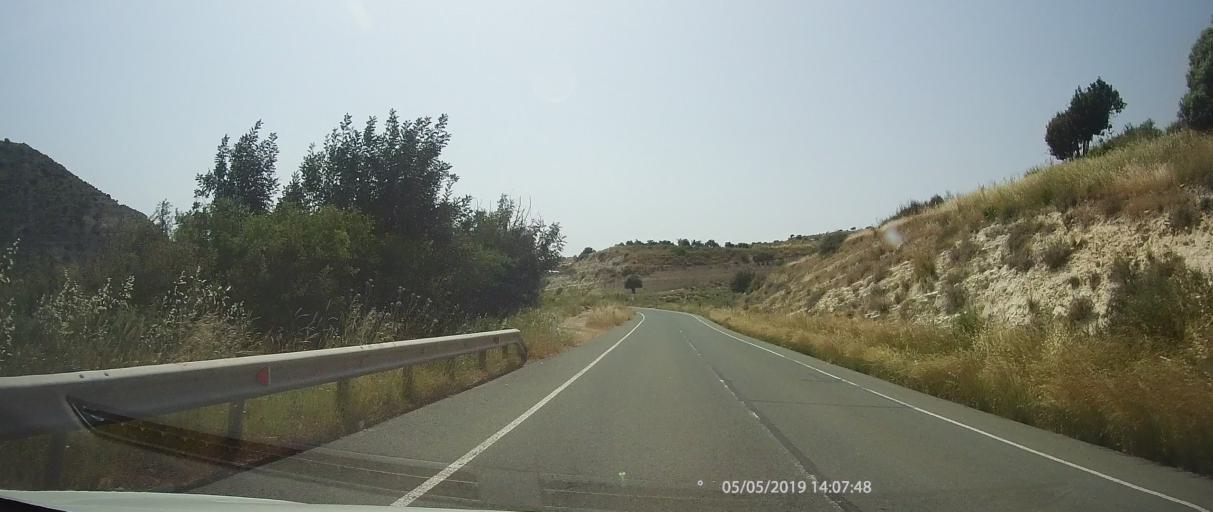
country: CY
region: Limassol
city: Pissouri
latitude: 34.7334
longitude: 32.5942
